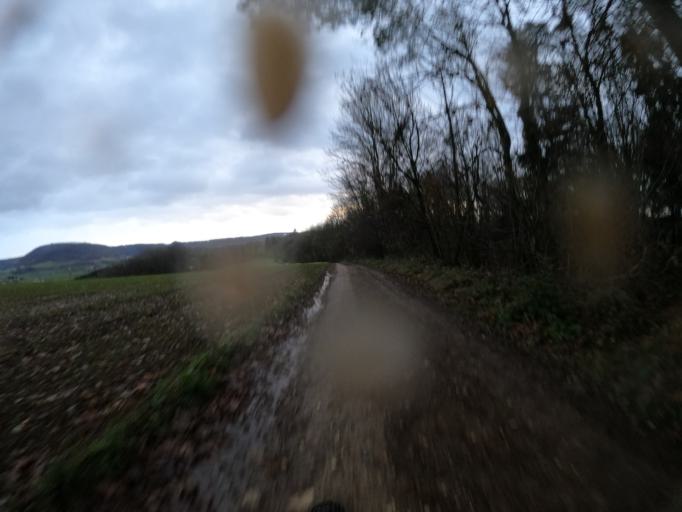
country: DE
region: Baden-Wuerttemberg
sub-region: Regierungsbezirk Stuttgart
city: Sussen
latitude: 48.7006
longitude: 9.7794
